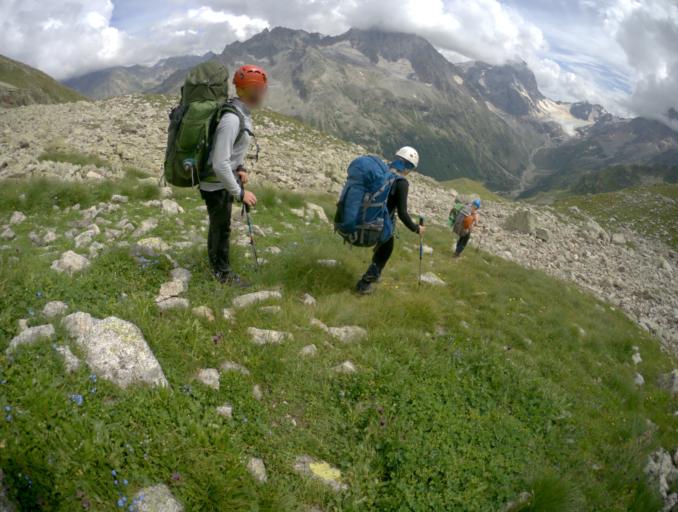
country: RU
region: Karachayevo-Cherkesiya
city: Uchkulan
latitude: 43.2722
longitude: 42.1243
